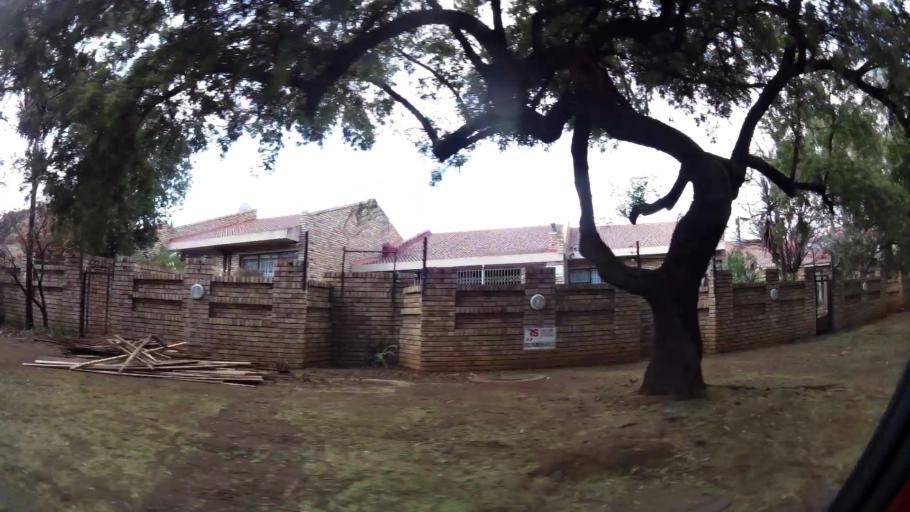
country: ZA
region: Gauteng
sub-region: Sedibeng District Municipality
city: Vanderbijlpark
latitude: -26.7443
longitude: 27.8286
